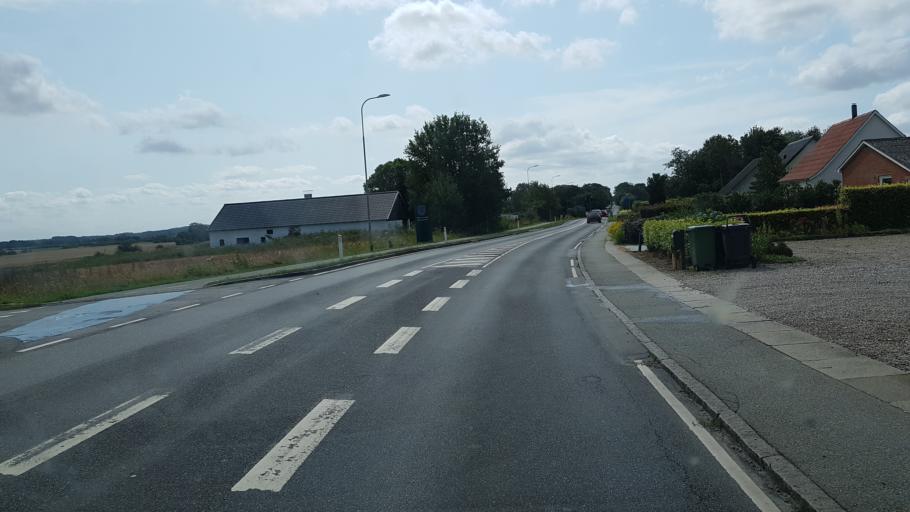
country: DK
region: South Denmark
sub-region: Vejen Kommune
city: Vejen
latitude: 55.5671
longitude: 9.1353
